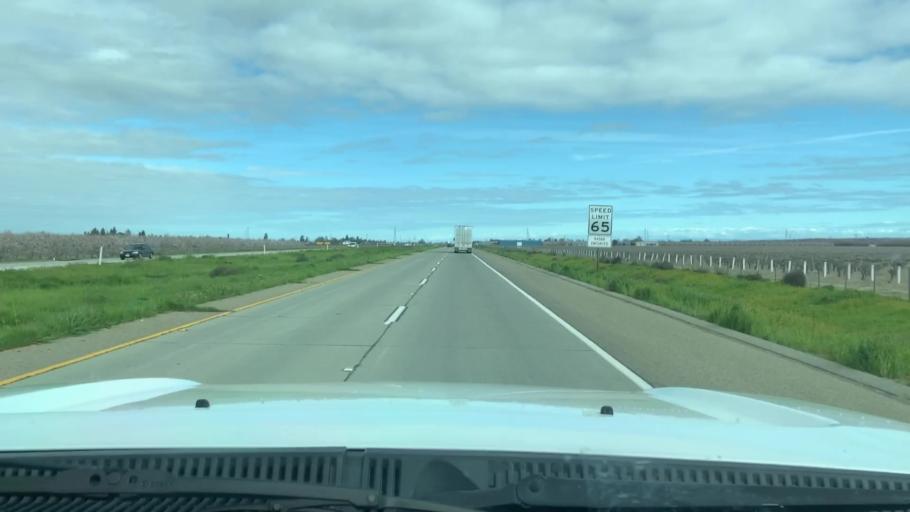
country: US
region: California
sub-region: Fresno County
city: Caruthers
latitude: 36.5771
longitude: -119.7859
